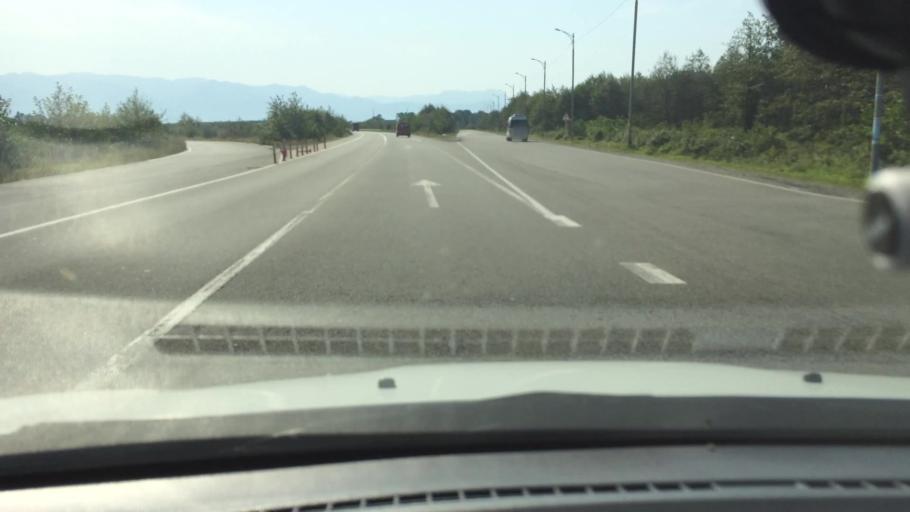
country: GE
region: Guria
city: Urek'i
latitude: 41.9242
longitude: 41.7736
